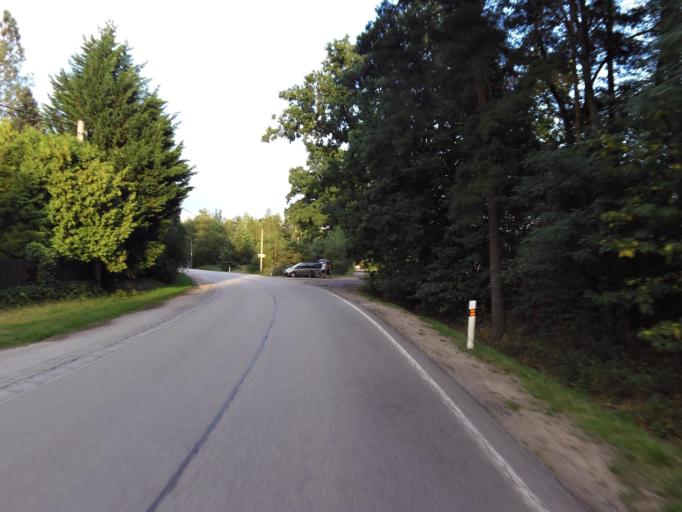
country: CZ
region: Jihocesky
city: Chlum u Trebone
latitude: 48.9480
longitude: 14.8755
